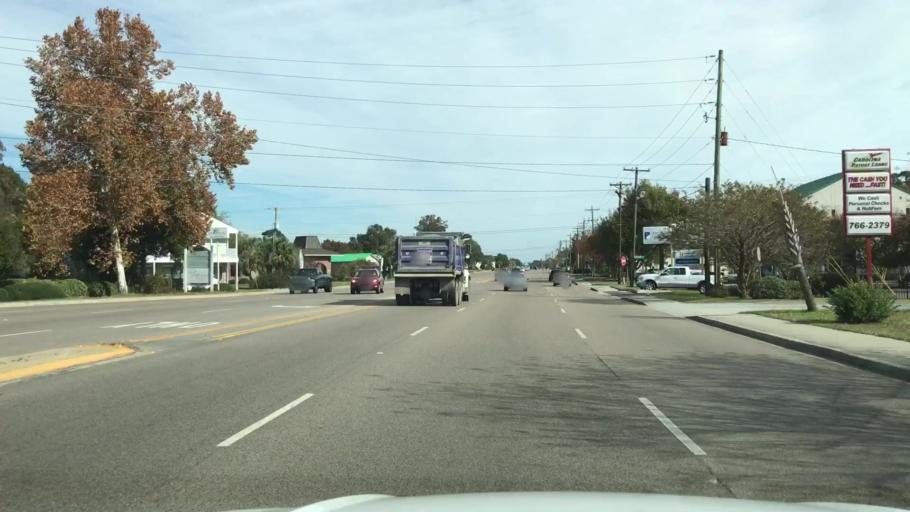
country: US
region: South Carolina
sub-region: Charleston County
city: North Charleston
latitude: 32.7966
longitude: -80.0255
